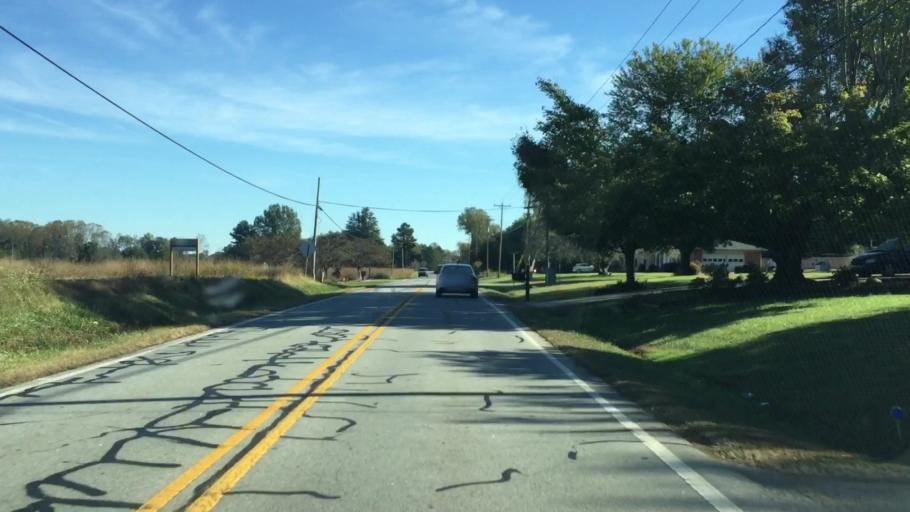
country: US
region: North Carolina
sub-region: Rowan County
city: Salisbury
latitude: 35.6578
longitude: -80.5630
